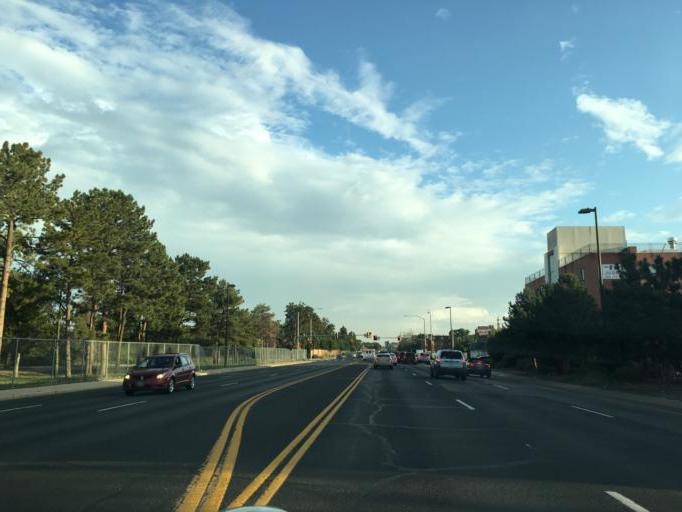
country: US
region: Colorado
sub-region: Adams County
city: Aurora
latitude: 39.7452
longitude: -104.8470
